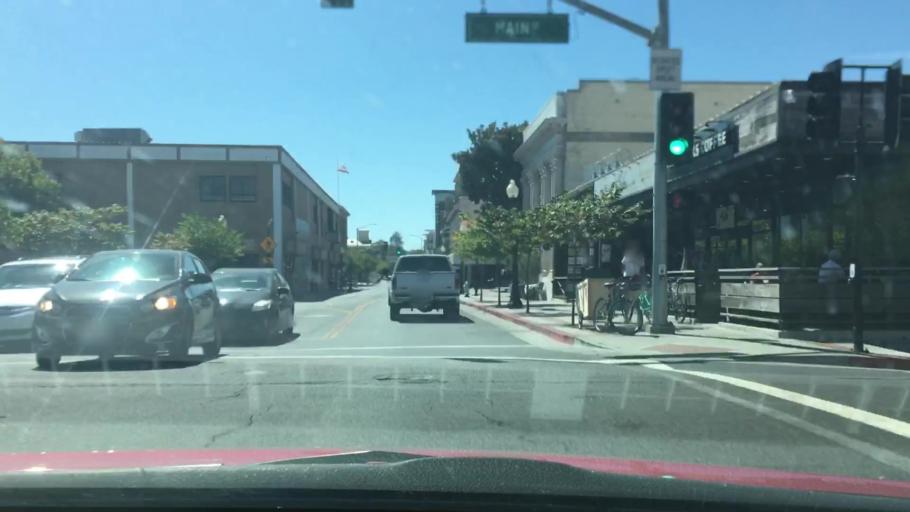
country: US
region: California
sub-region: Napa County
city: Napa
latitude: 38.2993
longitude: -122.2855
